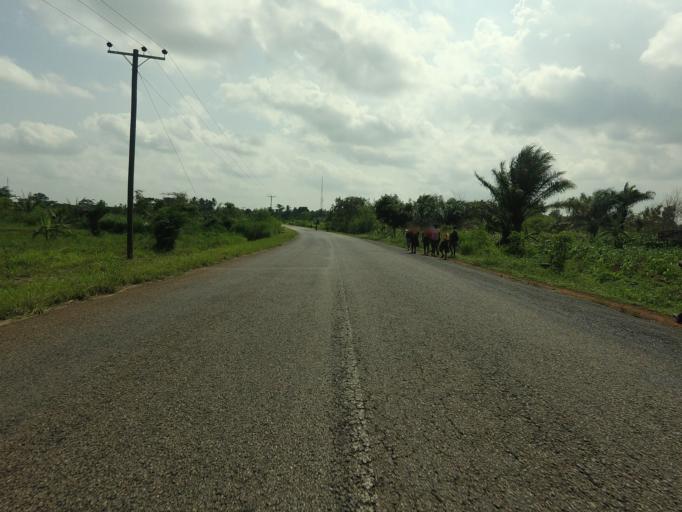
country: GH
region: Volta
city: Ho
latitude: 6.4160
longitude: 0.7532
